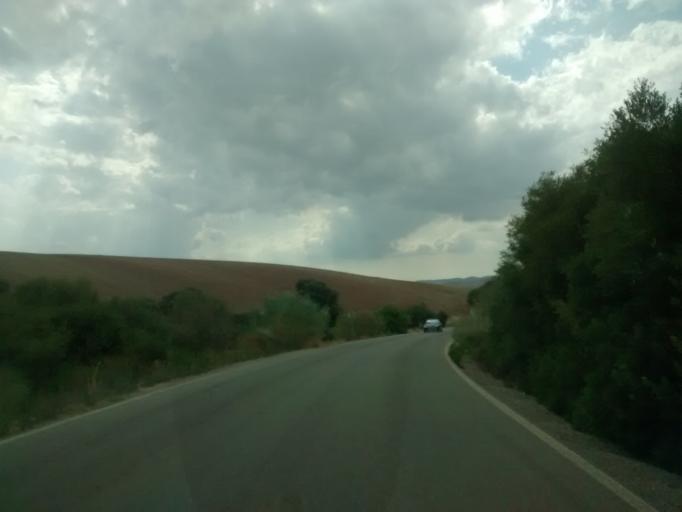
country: ES
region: Andalusia
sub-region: Provincia de Cadiz
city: Prado del Rey
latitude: 36.8293
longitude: -5.5859
